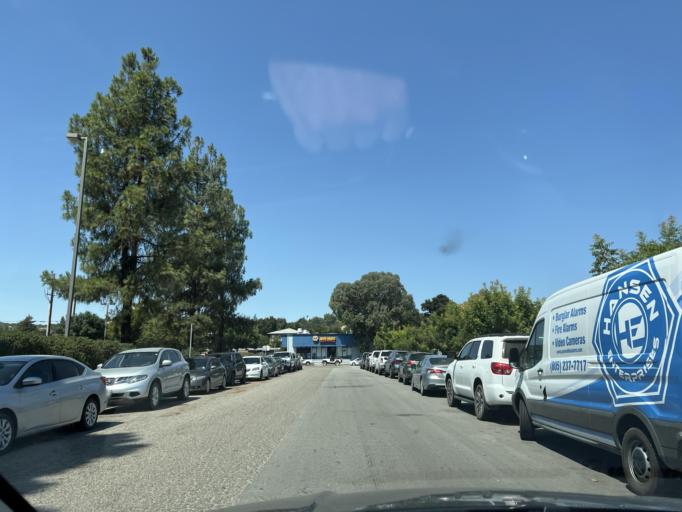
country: US
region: California
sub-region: San Luis Obispo County
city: Paso Robles
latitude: 35.6445
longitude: -120.6881
